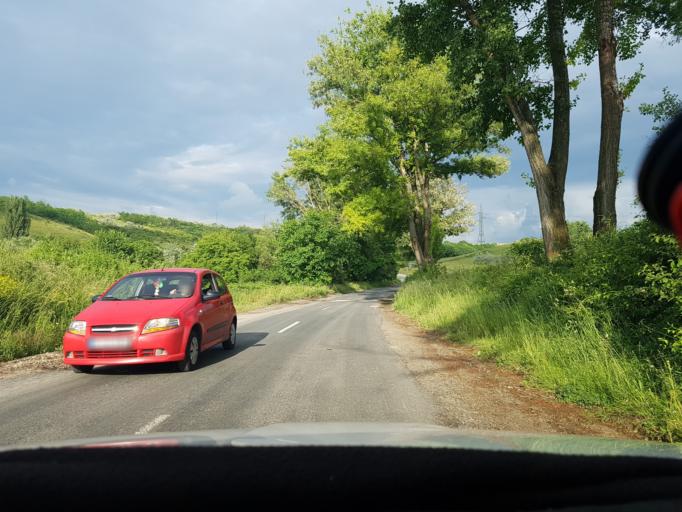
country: HU
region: Komarom-Esztergom
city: Labatlan
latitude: 47.7382
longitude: 18.5145
